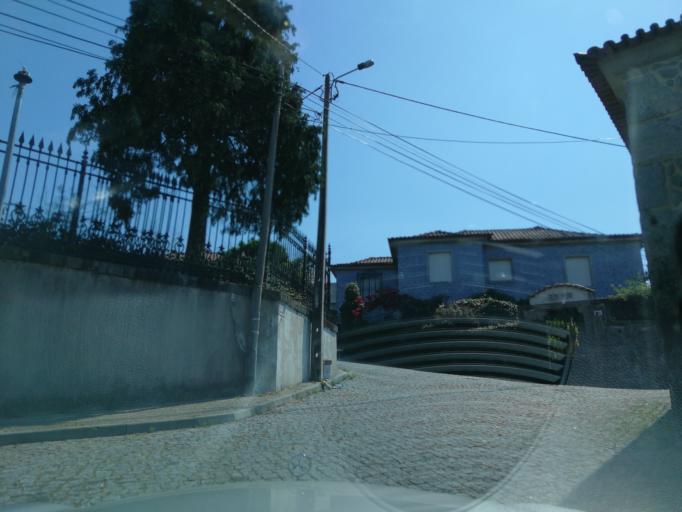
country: PT
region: Braga
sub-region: Braga
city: Adaufe
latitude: 41.5620
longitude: -8.3911
